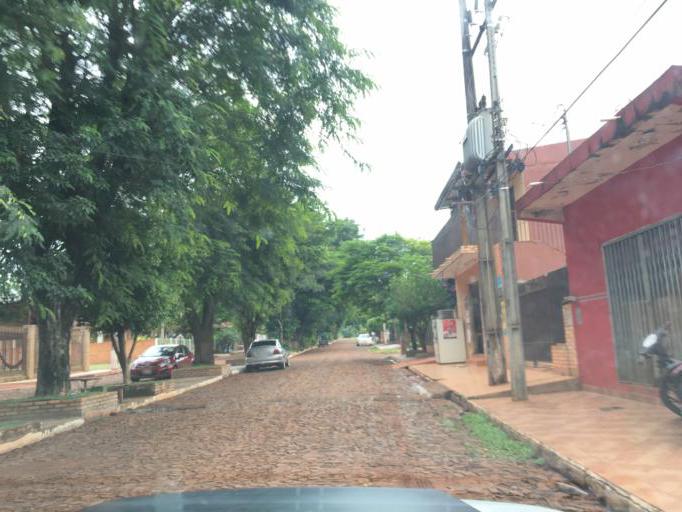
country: PY
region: Alto Parana
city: Ciudad del Este
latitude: -25.4209
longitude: -54.6431
